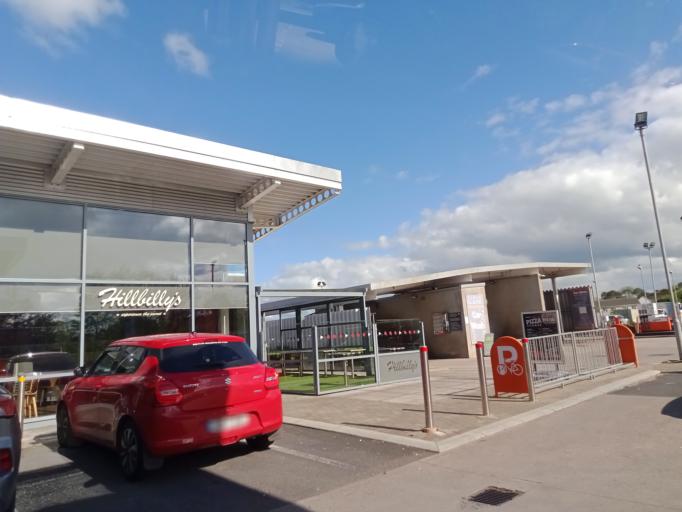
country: IE
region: Munster
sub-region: County Cork
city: Fermoy
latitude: 52.1509
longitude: -8.2784
